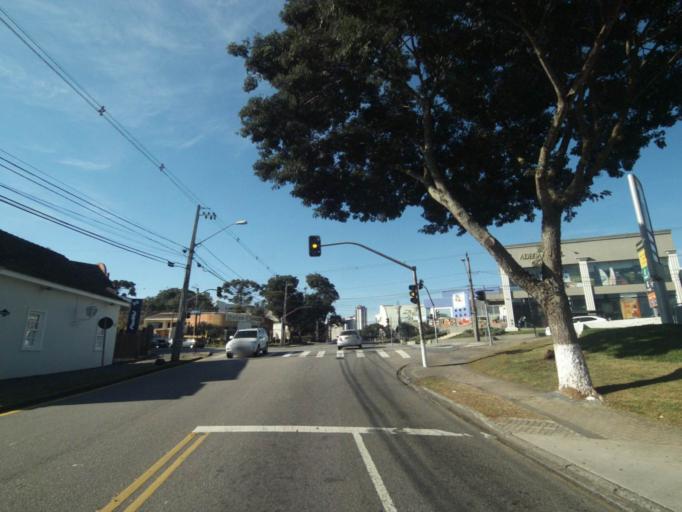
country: BR
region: Parana
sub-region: Curitiba
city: Curitiba
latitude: -25.4259
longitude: -49.2999
